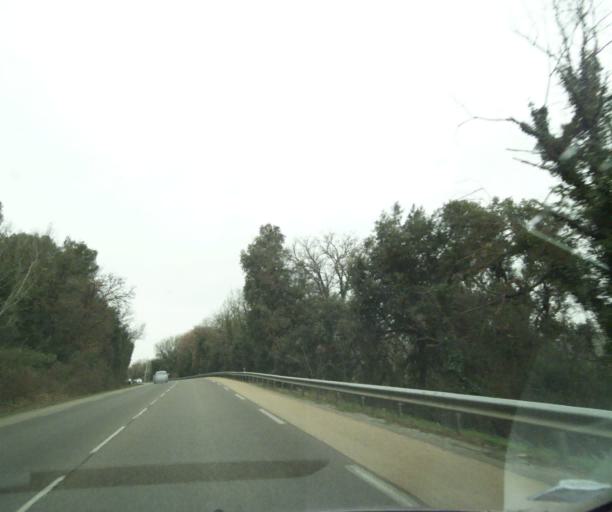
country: FR
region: Provence-Alpes-Cote d'Azur
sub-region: Departement des Bouches-du-Rhone
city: Jouques
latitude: 43.6563
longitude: 5.6255
